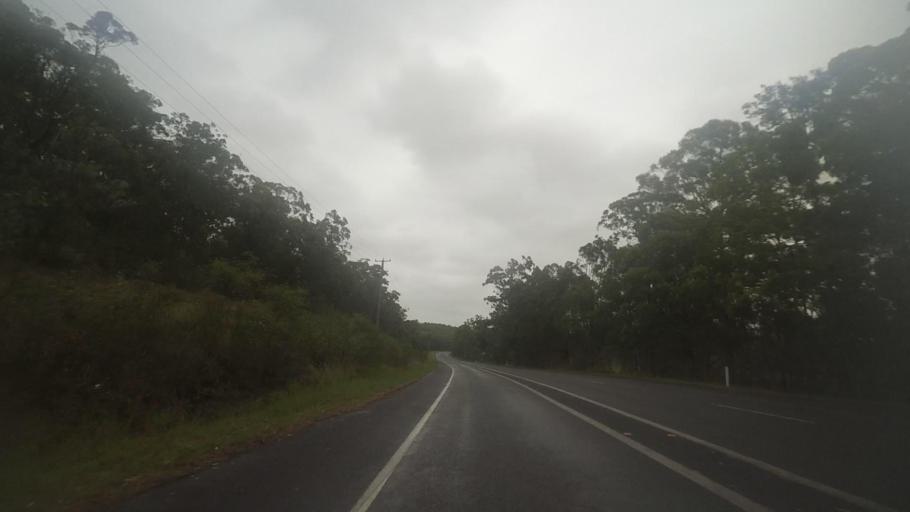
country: AU
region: New South Wales
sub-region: Port Stephens Shire
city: Port Stephens
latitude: -32.6448
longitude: 151.9832
